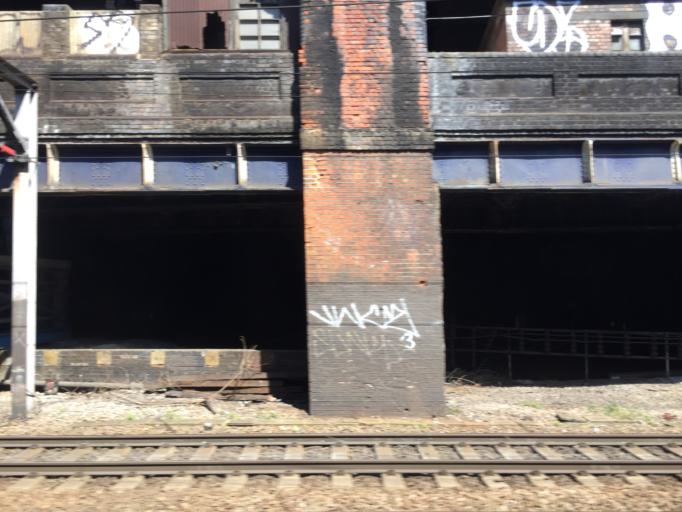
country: GB
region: England
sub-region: Greater London
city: Bethnal Green
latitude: 51.5225
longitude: -0.0740
